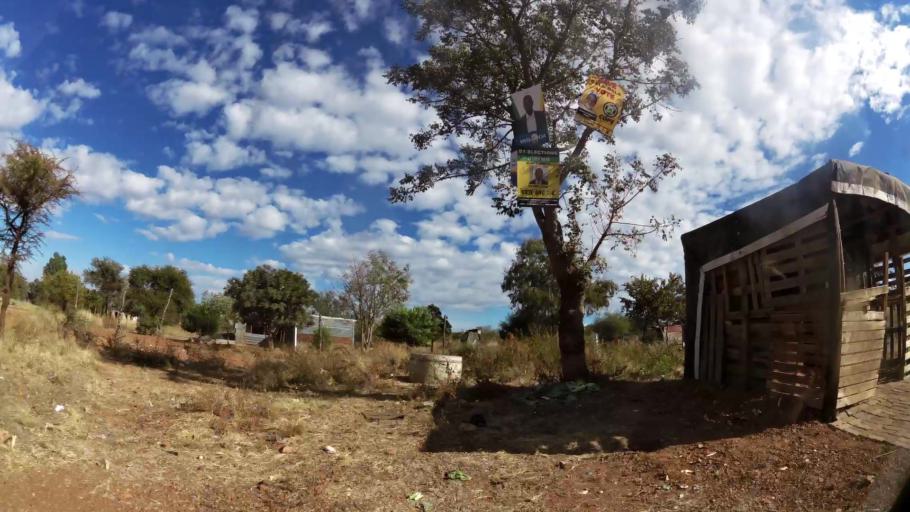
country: ZA
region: Limpopo
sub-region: Waterberg District Municipality
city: Warmbaths
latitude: -24.8751
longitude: 28.2735
